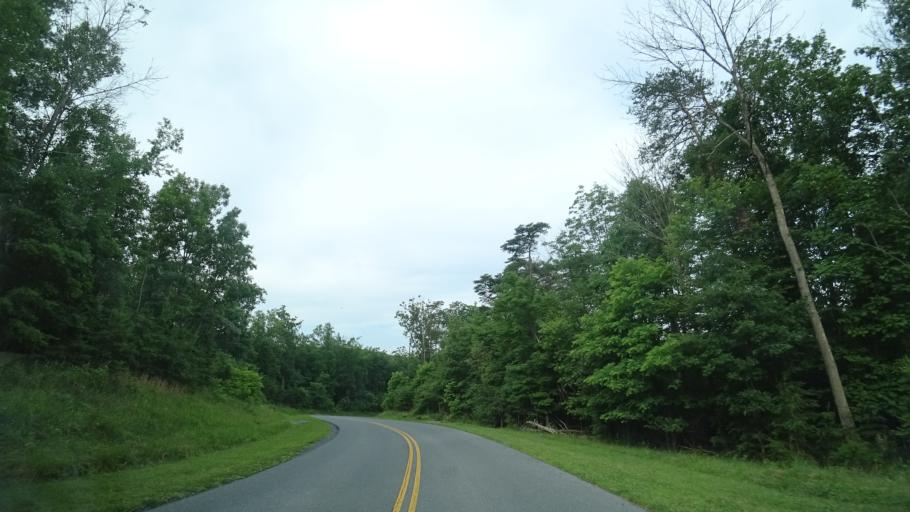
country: US
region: Virginia
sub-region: Warren County
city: Front Royal
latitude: 38.8475
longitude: -78.3089
